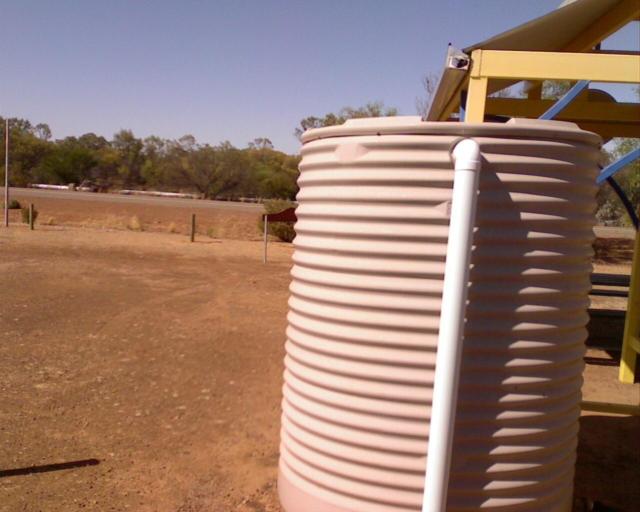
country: AU
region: Western Australia
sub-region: Wongan-Ballidu
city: Wongan Hills
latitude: -30.5972
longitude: 116.7690
